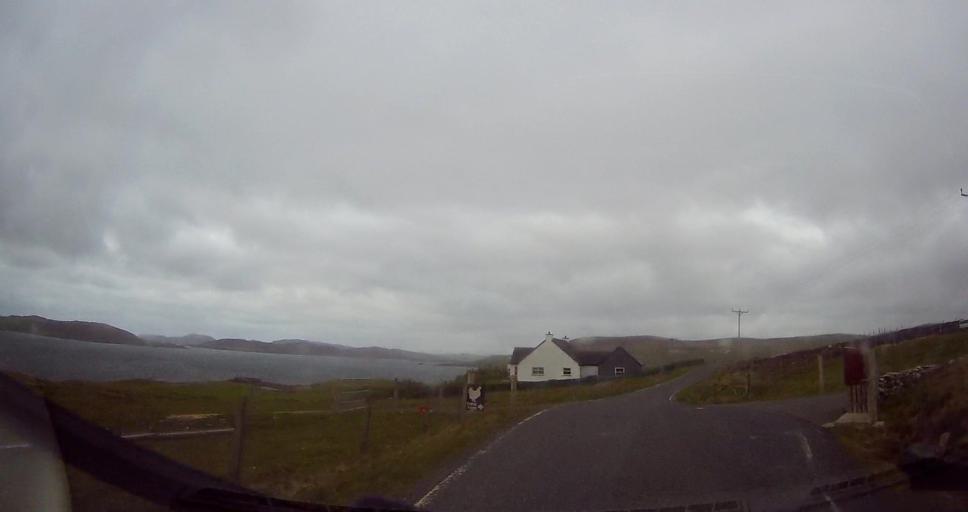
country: GB
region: Scotland
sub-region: Shetland Islands
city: Lerwick
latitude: 60.2957
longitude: -1.3639
